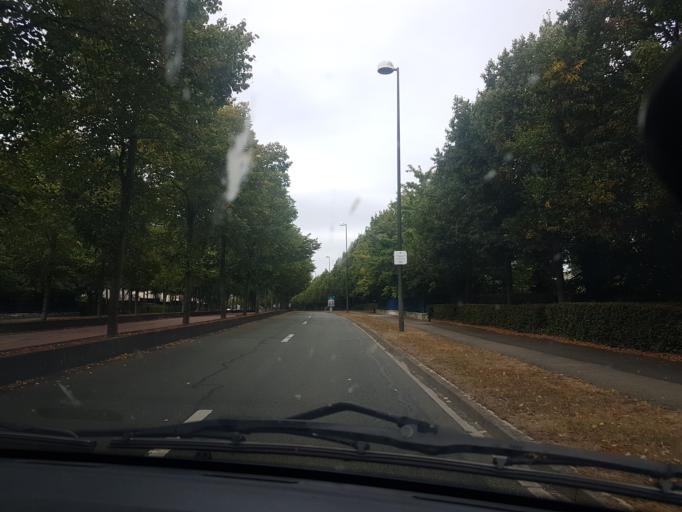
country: FR
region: Ile-de-France
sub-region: Departement des Yvelines
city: Guyancourt
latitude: 48.7676
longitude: 2.0648
